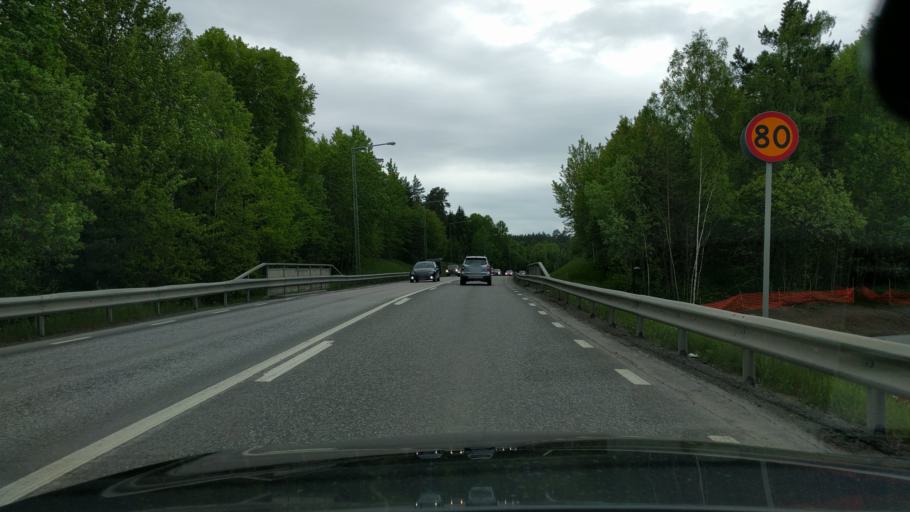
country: SE
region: Stockholm
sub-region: Taby Kommun
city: Taby
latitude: 59.4648
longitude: 18.1195
